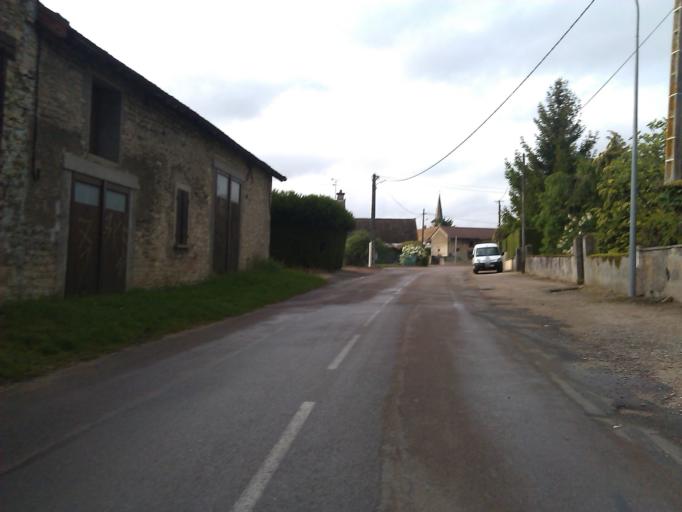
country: FR
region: Bourgogne
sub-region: Departement de Saone-et-Loire
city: Crissey
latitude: 46.8141
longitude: 4.8837
